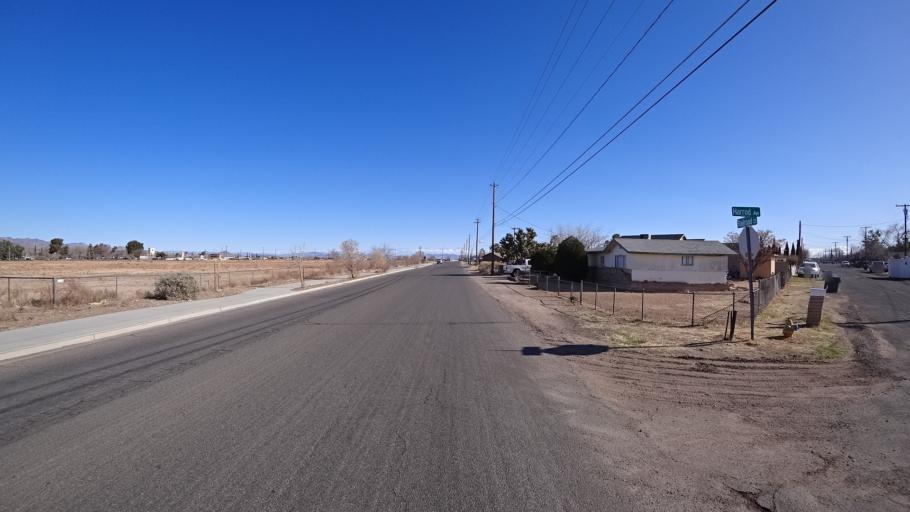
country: US
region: Arizona
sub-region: Mohave County
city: Kingman
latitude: 35.1980
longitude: -114.0244
